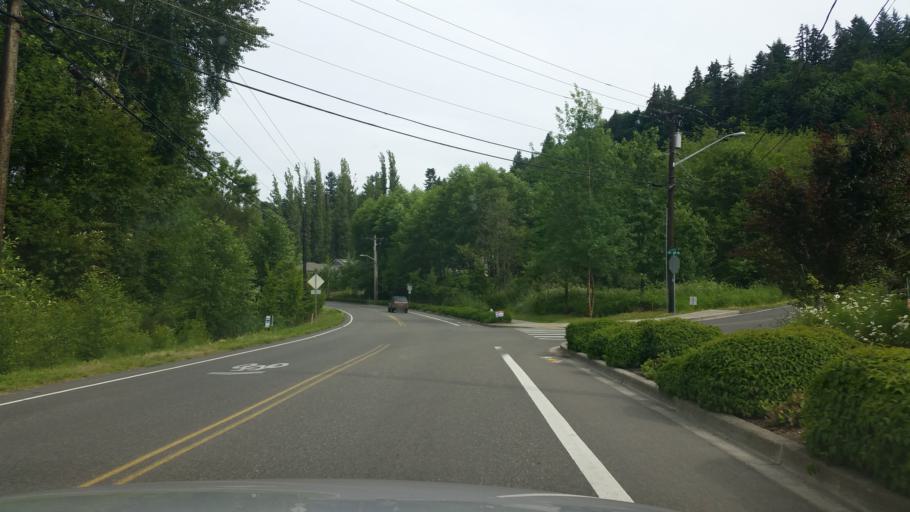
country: US
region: Washington
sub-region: King County
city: Bothell
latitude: 47.7541
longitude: -122.1965
